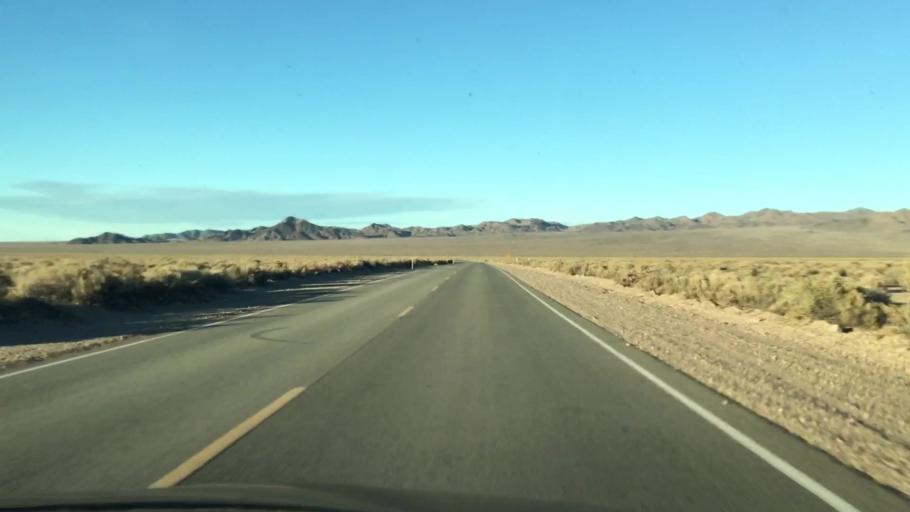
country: US
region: California
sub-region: San Bernardino County
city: Fort Irwin
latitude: 35.3238
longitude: -116.0817
